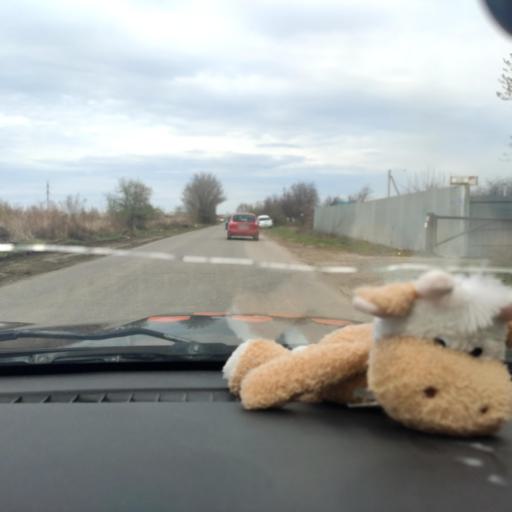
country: RU
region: Samara
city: Podstepki
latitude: 53.5955
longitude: 49.2283
